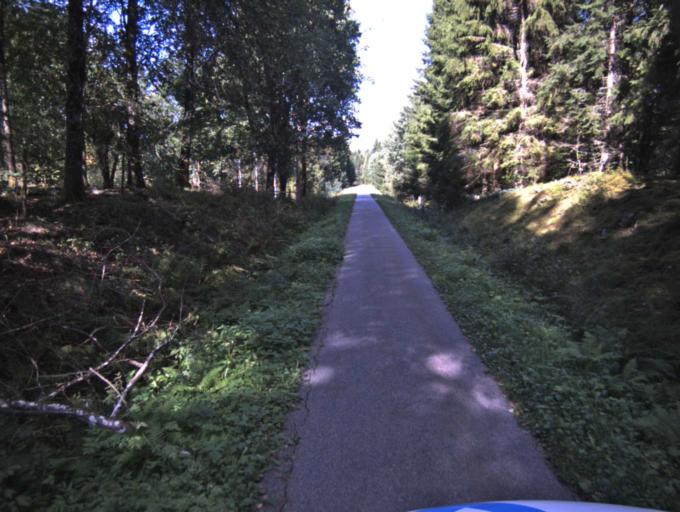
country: SE
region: Vaestra Goetaland
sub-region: Ulricehamns Kommun
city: Ulricehamn
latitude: 57.8262
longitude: 13.3457
